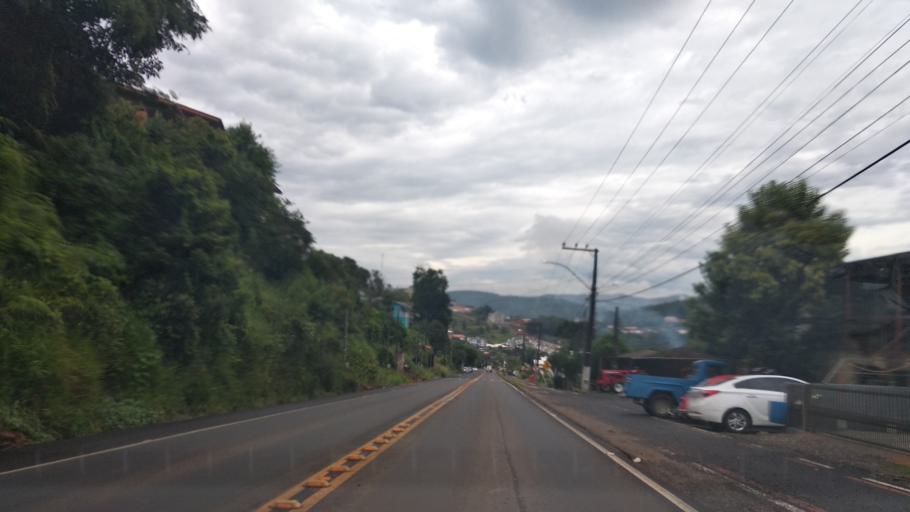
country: BR
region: Santa Catarina
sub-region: Videira
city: Videira
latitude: -27.0911
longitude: -51.2442
